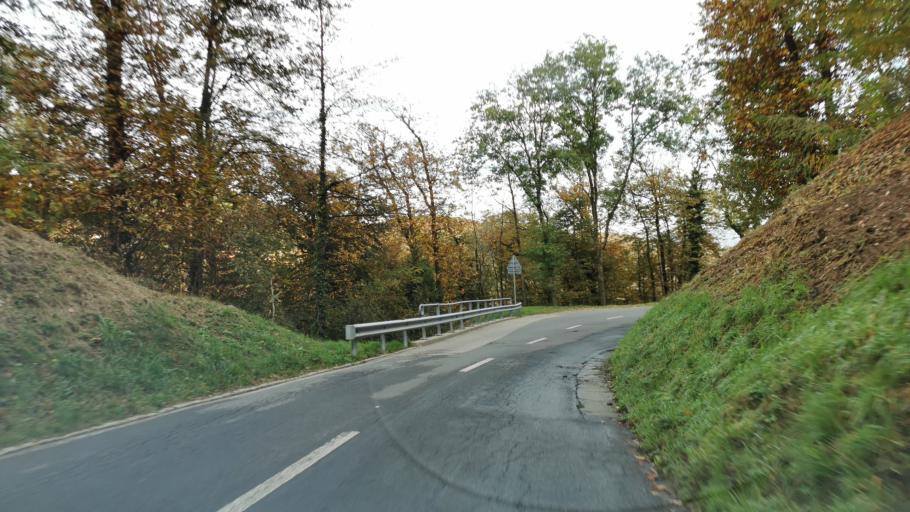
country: CH
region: Ticino
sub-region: Lugano District
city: Pura
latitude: 46.0170
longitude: 8.8545
